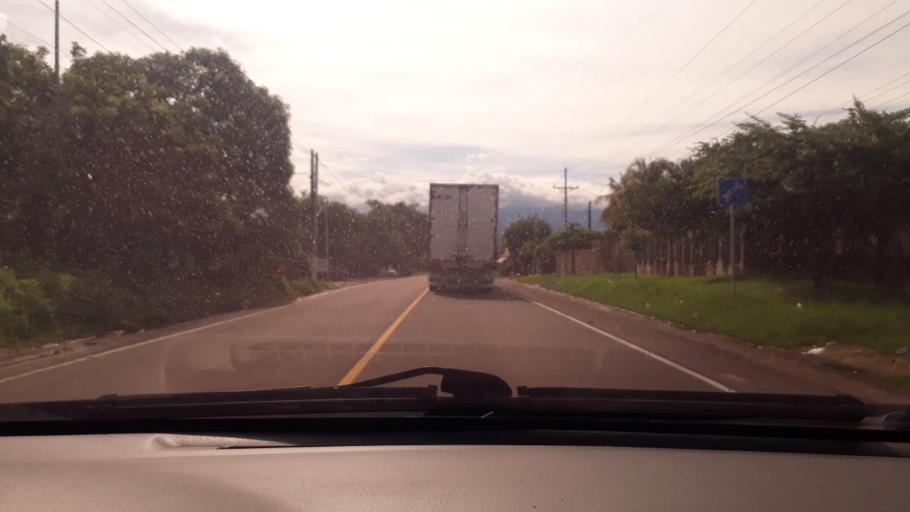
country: SV
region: Ahuachapan
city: San Francisco Menendez
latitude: 13.8793
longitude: -90.1150
